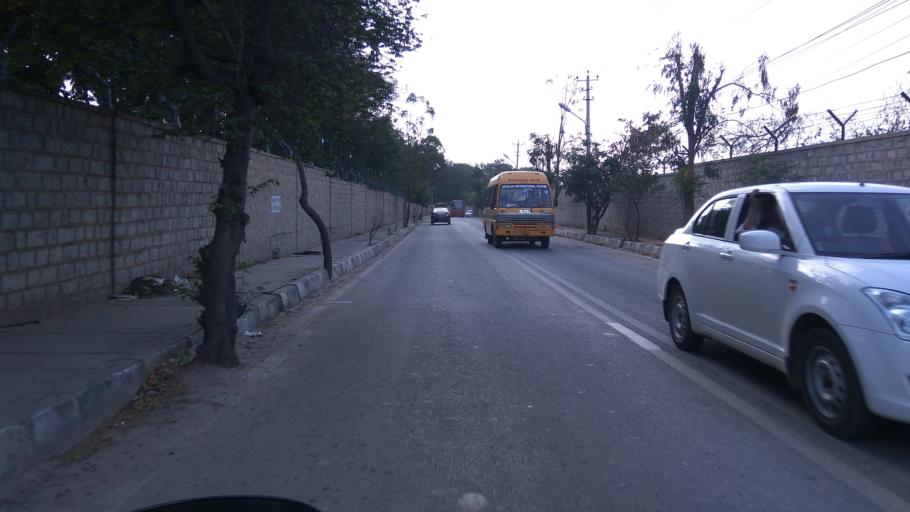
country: IN
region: Karnataka
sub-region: Bangalore Urban
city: Bangalore
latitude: 12.9676
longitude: 77.6979
